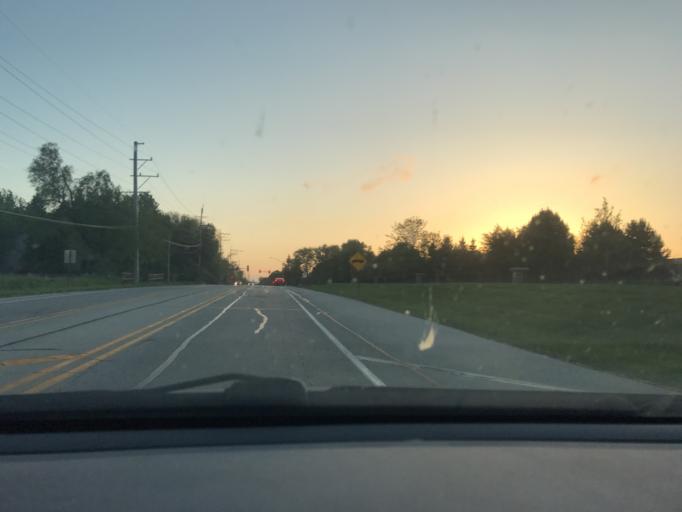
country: US
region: Illinois
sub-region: Kane County
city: South Elgin
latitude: 42.0068
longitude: -88.3574
